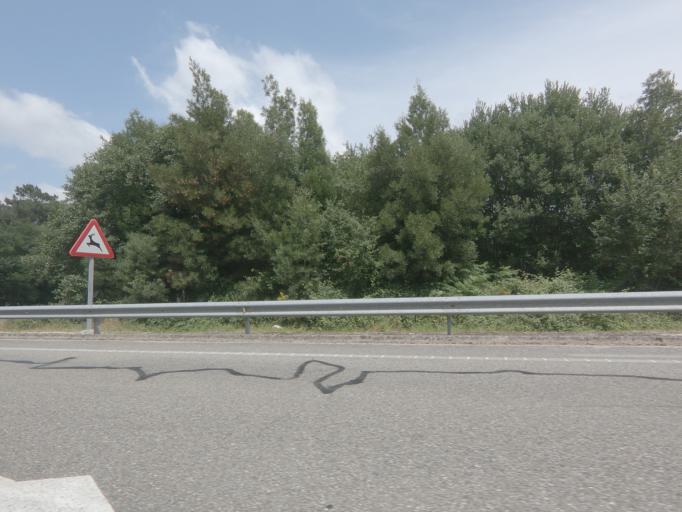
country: ES
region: Galicia
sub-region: Provincia de Pontevedra
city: Tomino
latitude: 42.0214
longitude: -8.7327
